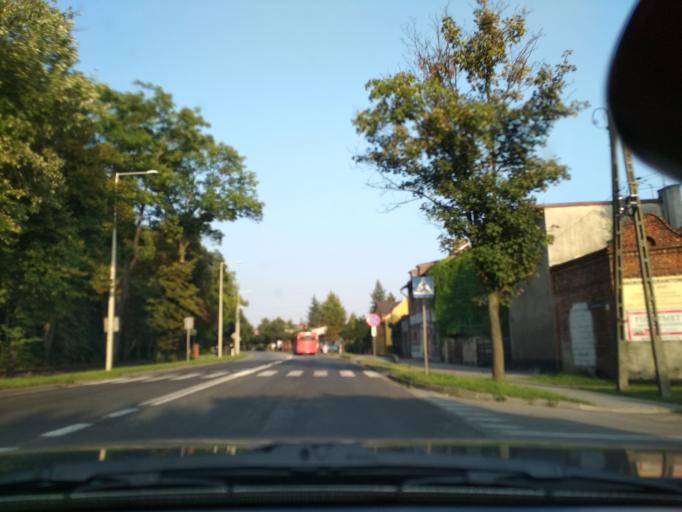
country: PL
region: Silesian Voivodeship
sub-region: Powiat zawiercianski
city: Zawiercie
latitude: 50.4791
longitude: 19.4451
